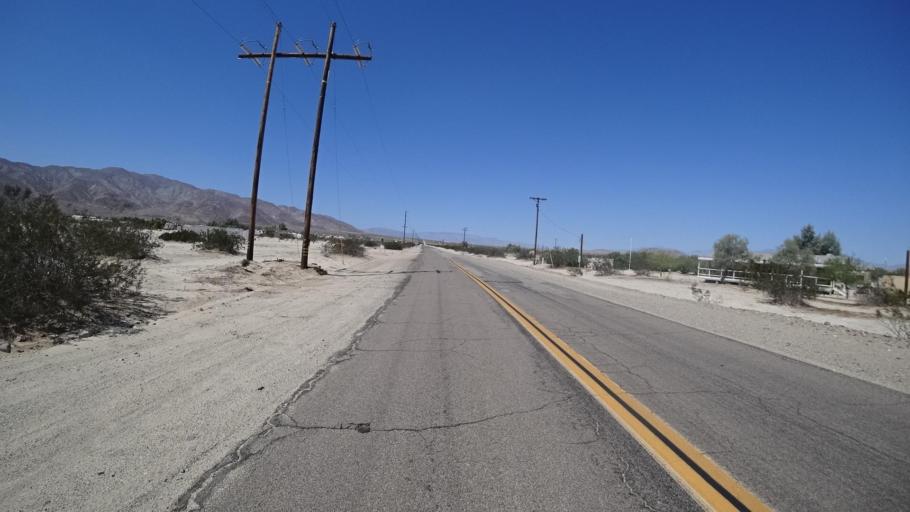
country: US
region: California
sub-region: Imperial County
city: Salton City
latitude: 33.1010
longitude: -116.1165
